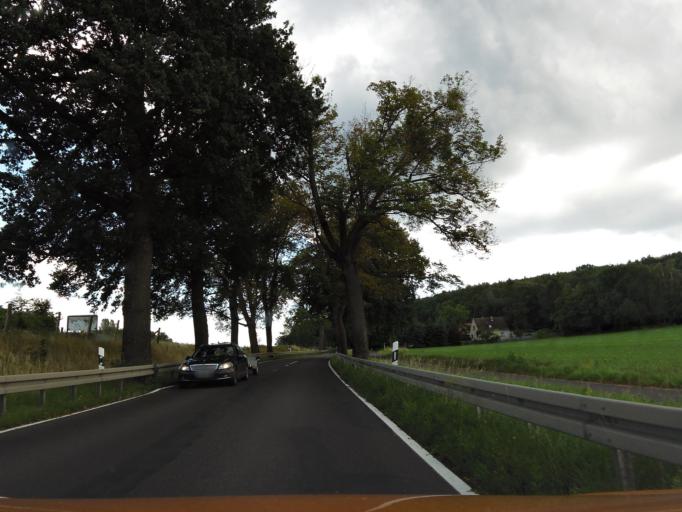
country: DE
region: Brandenburg
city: Potsdam
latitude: 52.4556
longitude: 13.0404
